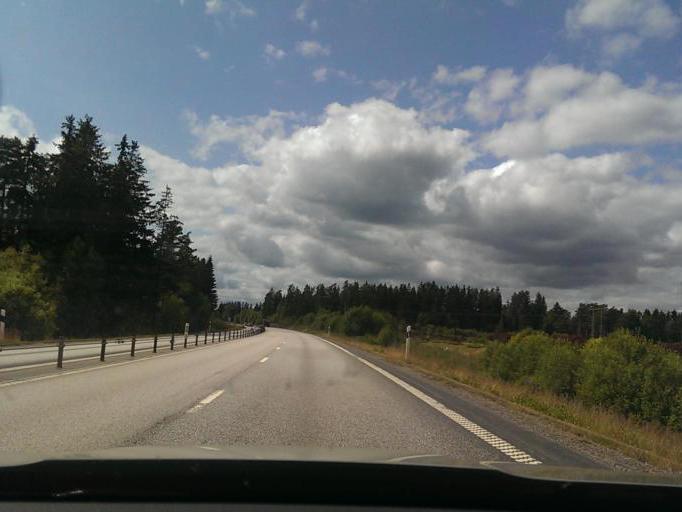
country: SE
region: Joenkoeping
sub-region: Varnamo Kommun
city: Varnamo
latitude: 57.1813
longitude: 13.9937
